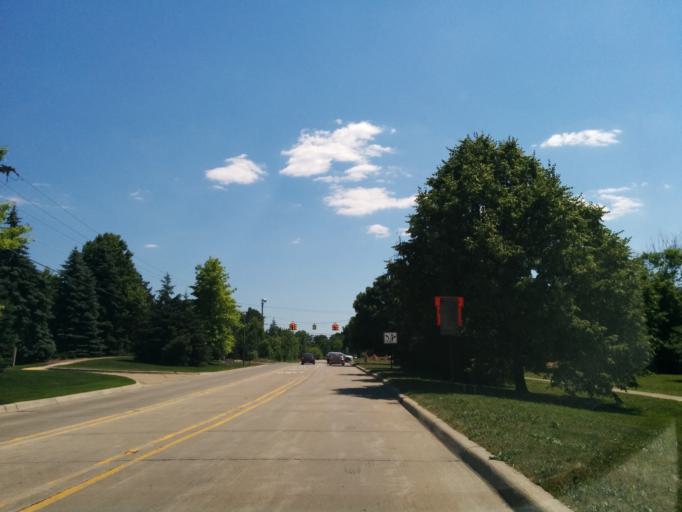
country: US
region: Michigan
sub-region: Oakland County
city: Farmington Hills
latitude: 42.5133
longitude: -83.4181
